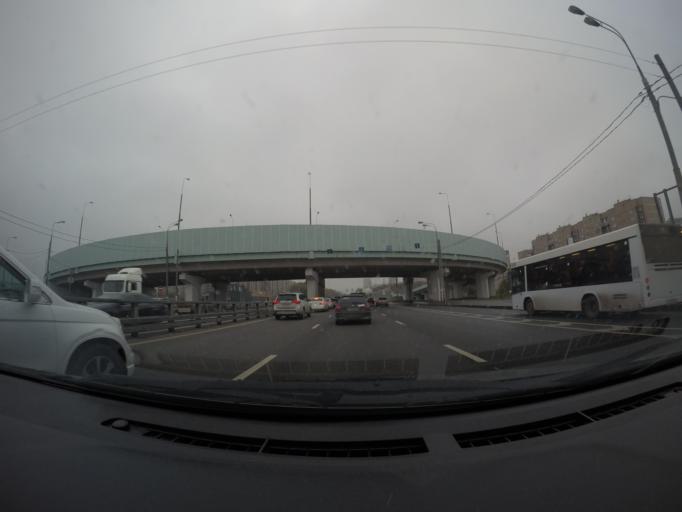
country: RU
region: Moskovskaya
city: Shcherbinka
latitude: 55.5336
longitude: 37.5818
